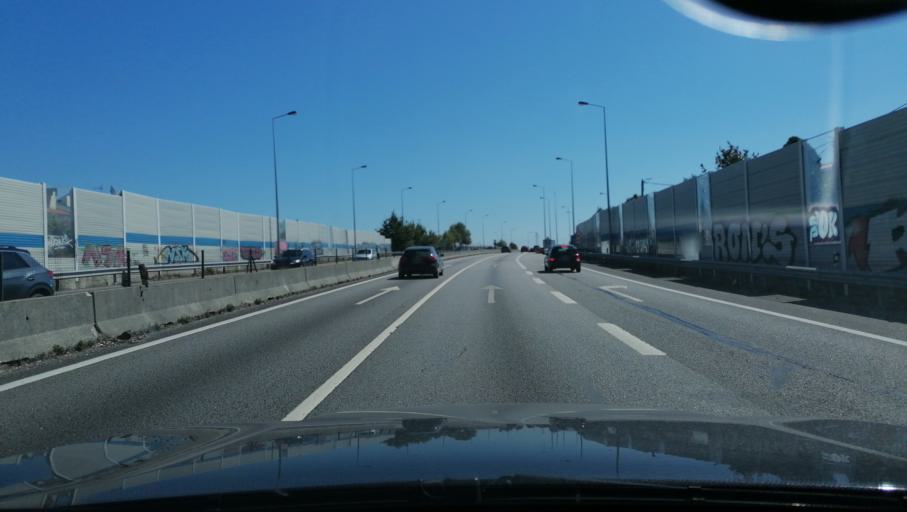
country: PT
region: Porto
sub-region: Vila Nova de Gaia
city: Vilar do Paraiso
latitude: 41.1003
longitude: -8.6265
